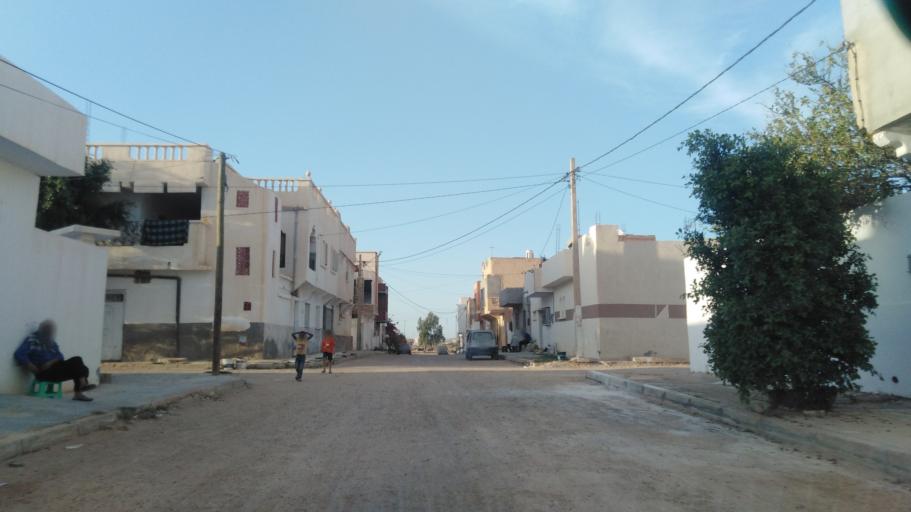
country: TN
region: Tataouine
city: Tataouine
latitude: 32.9420
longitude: 10.4576
